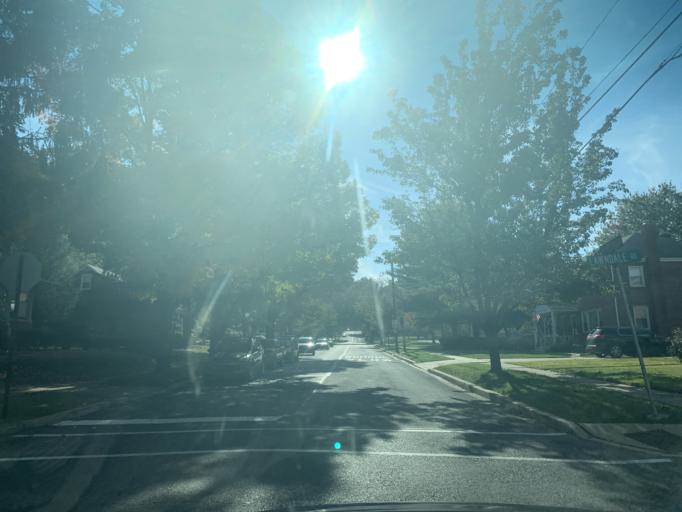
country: US
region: Pennsylvania
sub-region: Berks County
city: Wyomissing Hills
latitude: 40.3354
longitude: -75.9764
